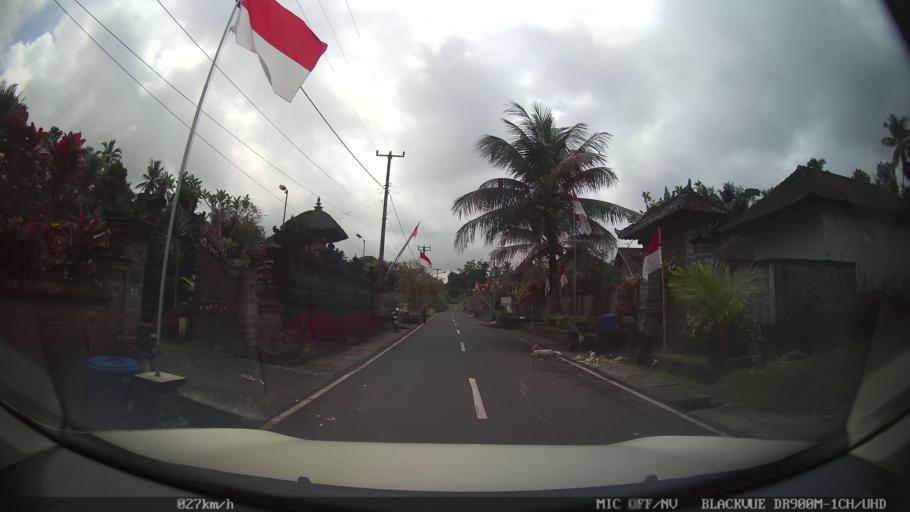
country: ID
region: Bali
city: Pemijian
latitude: -8.4541
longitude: 115.2302
